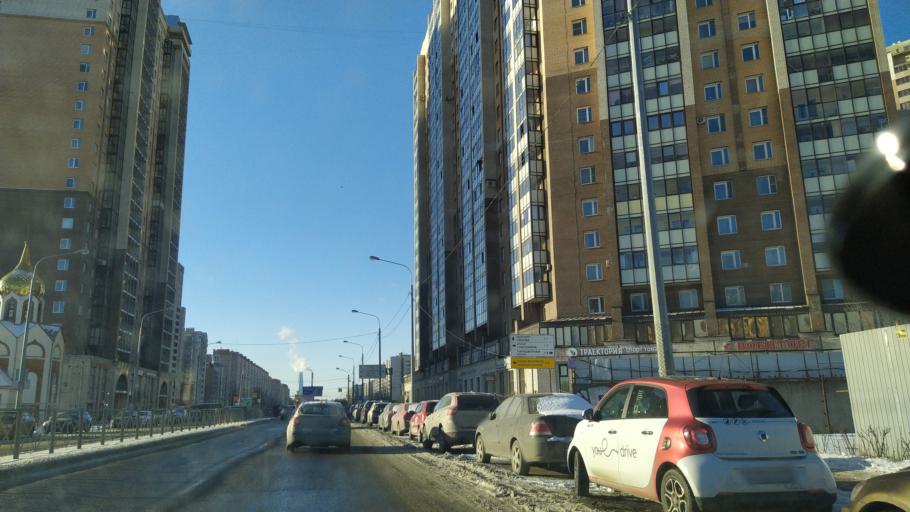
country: RU
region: Leningrad
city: Chernaya Rechka
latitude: 60.0012
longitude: 30.3026
